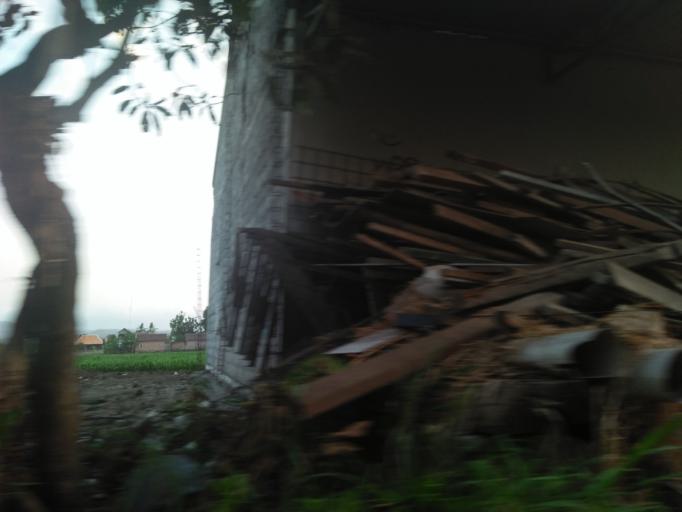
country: ID
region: Daerah Istimewa Yogyakarta
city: Sewon
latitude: -7.8569
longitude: 110.4138
